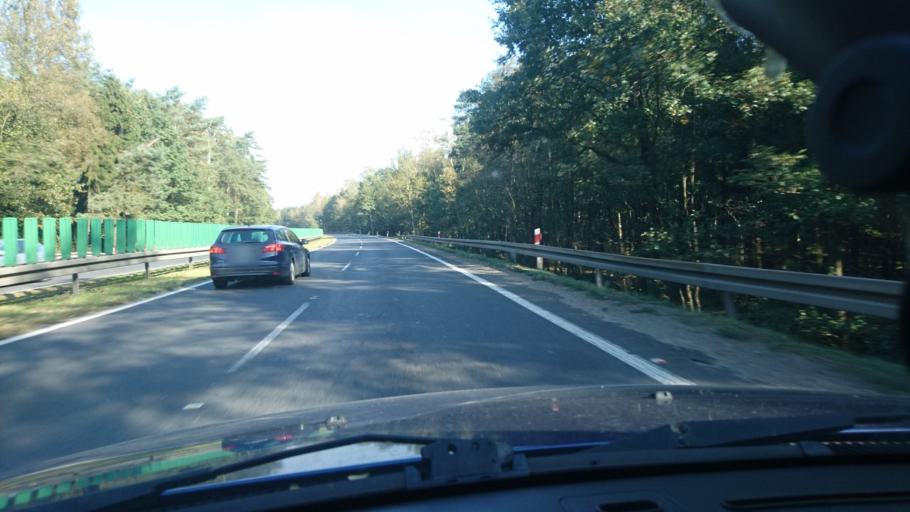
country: PL
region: Silesian Voivodeship
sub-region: Katowice
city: Murcki
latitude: 50.1517
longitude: 19.0244
